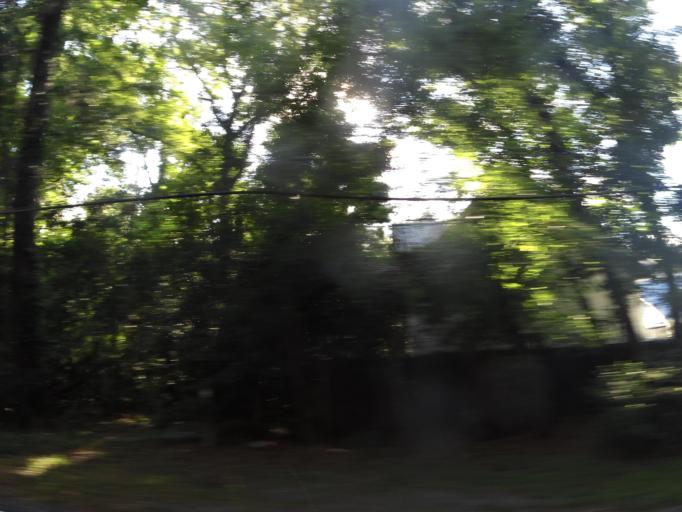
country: US
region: Georgia
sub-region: Glynn County
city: Saint Simon Mills
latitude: 31.2087
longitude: -81.3757
